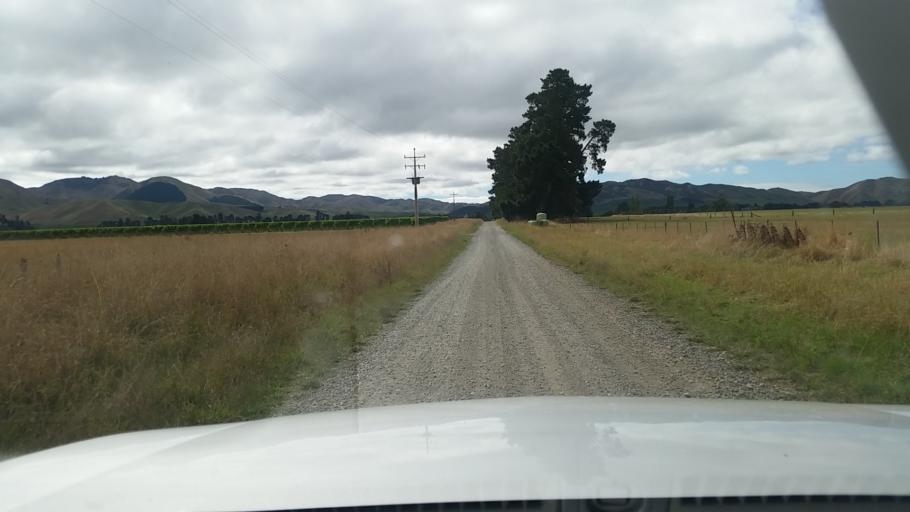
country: NZ
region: Marlborough
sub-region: Marlborough District
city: Blenheim
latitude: -41.6767
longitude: 174.0386
